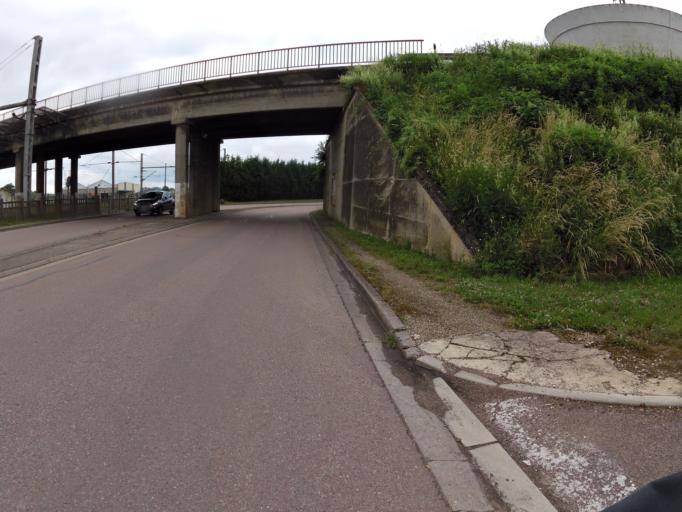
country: FR
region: Champagne-Ardenne
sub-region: Departement de la Haute-Marne
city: Saint-Dizier
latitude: 48.6468
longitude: 4.9343
